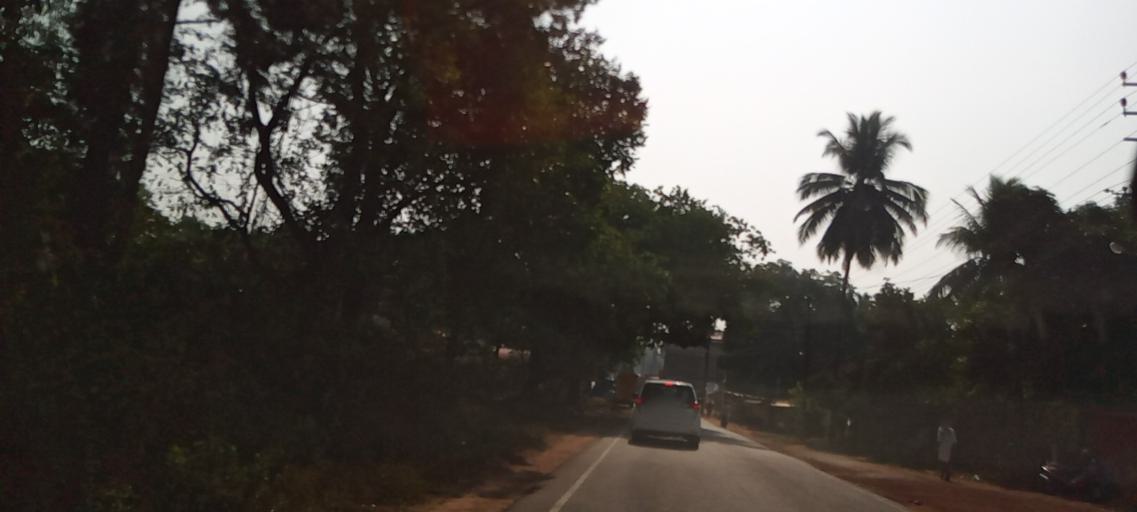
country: IN
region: Karnataka
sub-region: Udupi
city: Coondapoor
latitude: 13.5132
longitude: 74.7718
